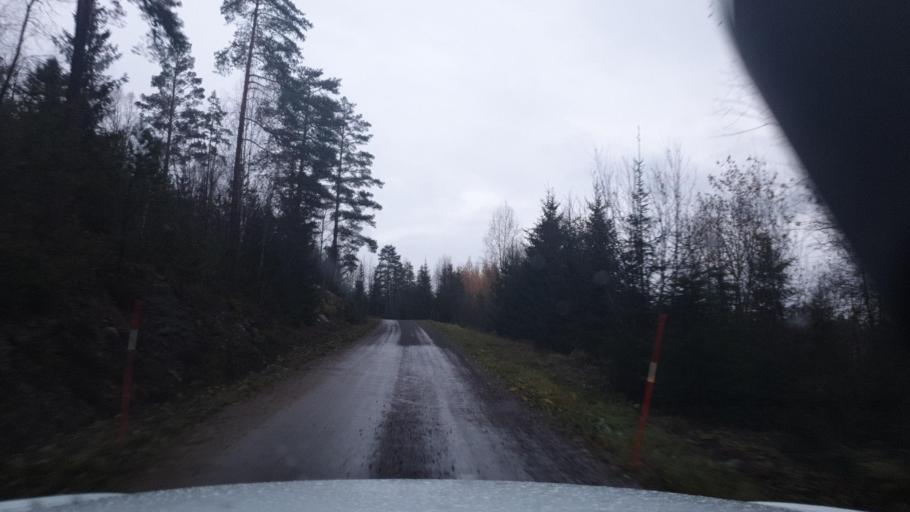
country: SE
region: Vaermland
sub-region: Eda Kommun
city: Amotfors
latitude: 59.8032
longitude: 12.4424
